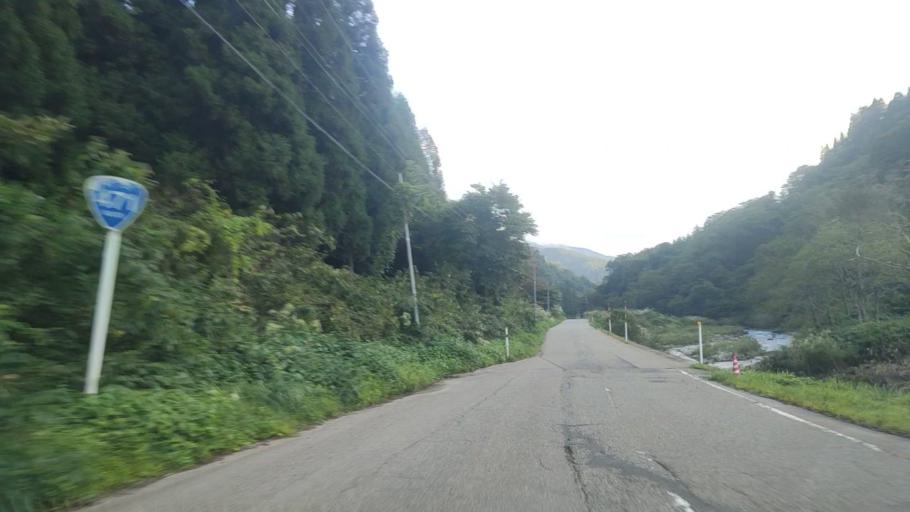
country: JP
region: Toyama
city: Yatsuomachi-higashikumisaka
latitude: 36.4785
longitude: 137.0492
